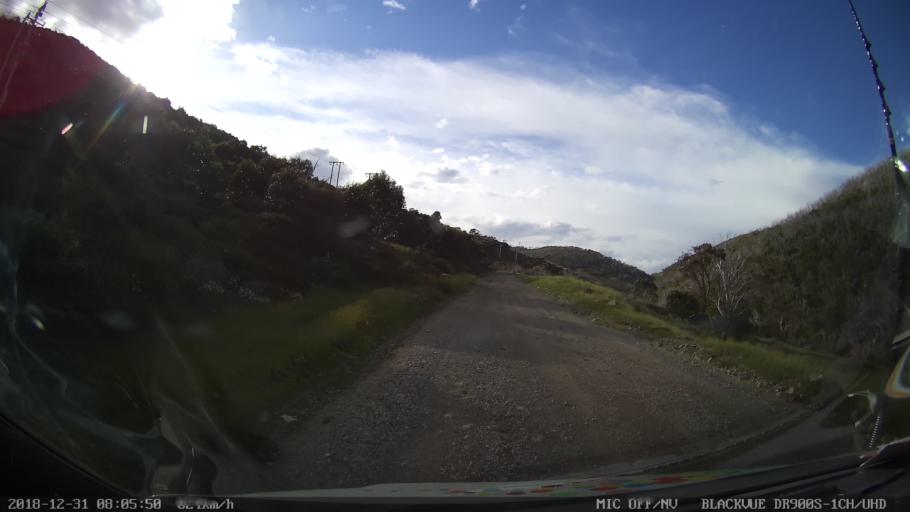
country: AU
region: New South Wales
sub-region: Snowy River
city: Jindabyne
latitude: -36.3725
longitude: 148.4071
